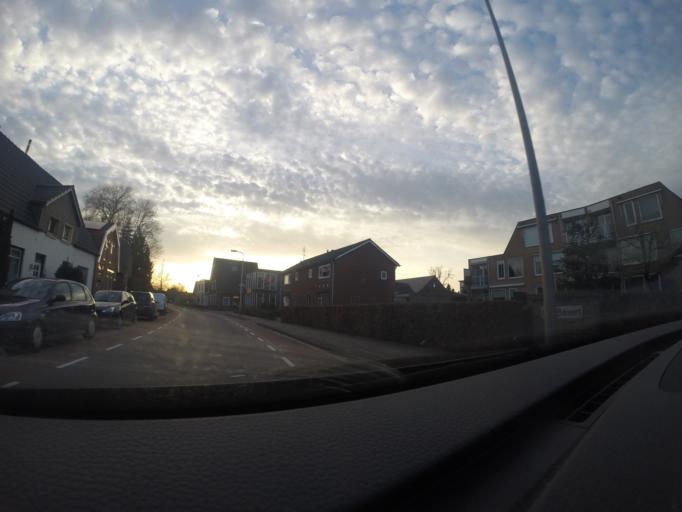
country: NL
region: Overijssel
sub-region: Gemeente Haaksbergen
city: Haaksbergen
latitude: 52.1545
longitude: 6.7478
